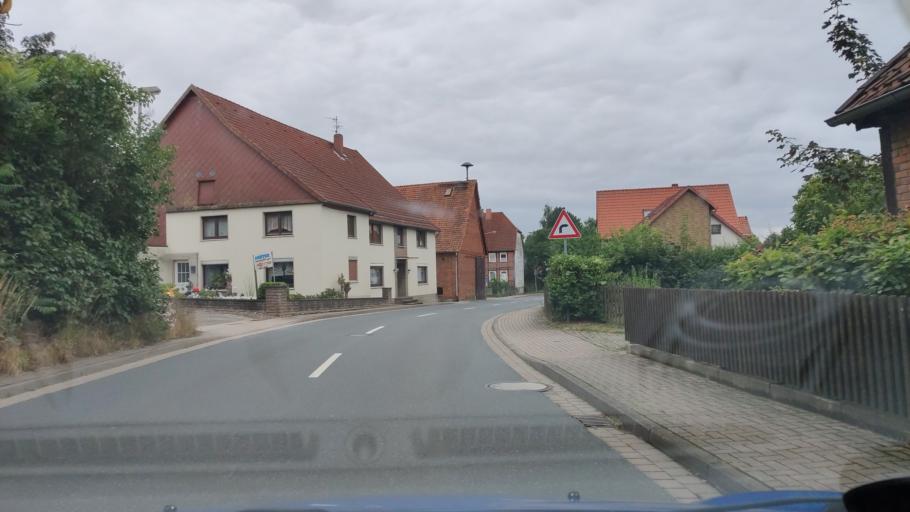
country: DE
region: Lower Saxony
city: Bad Munder am Deister
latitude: 52.1632
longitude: 9.4852
